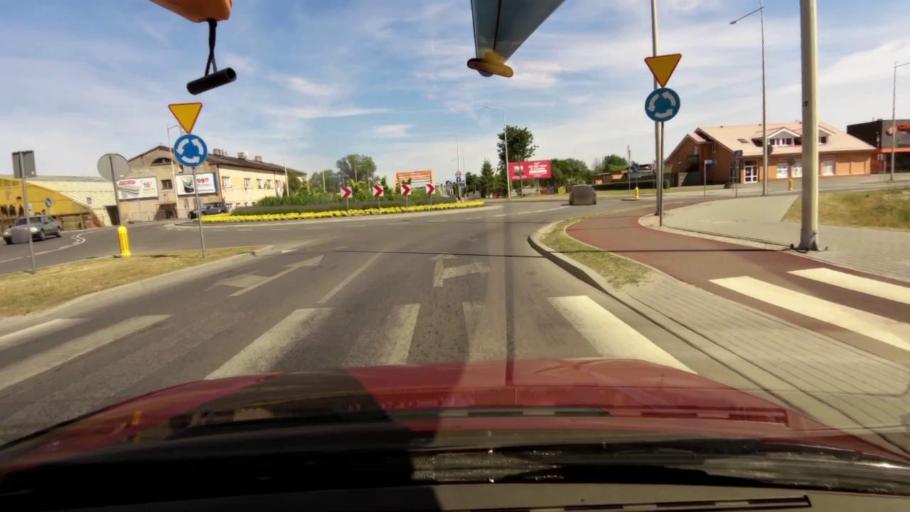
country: PL
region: Pomeranian Voivodeship
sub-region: Powiat slupski
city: Kobylnica
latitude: 54.4556
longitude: 17.0066
